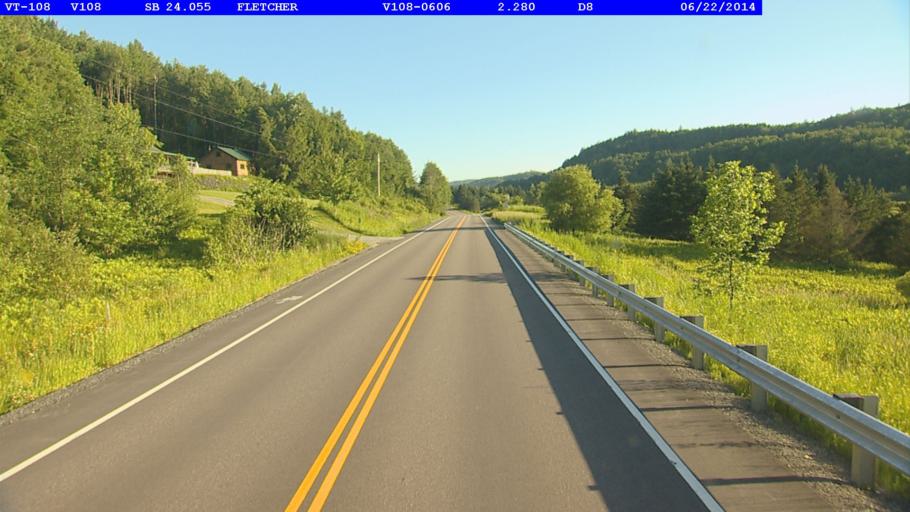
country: US
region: Vermont
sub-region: Franklin County
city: Enosburg Falls
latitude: 44.7329
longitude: -72.8278
